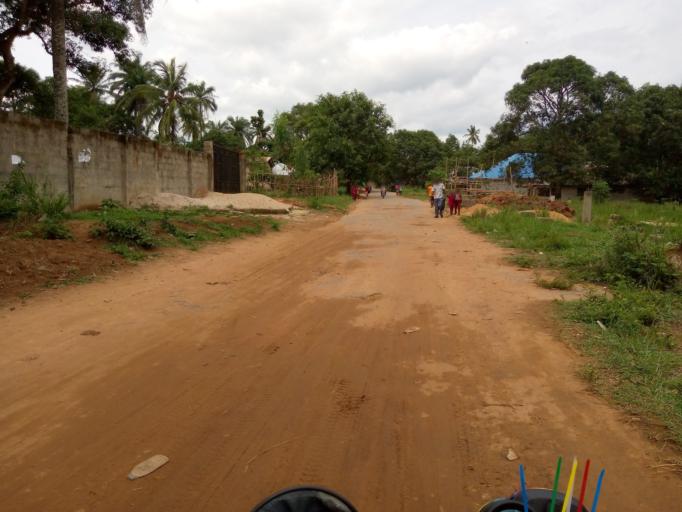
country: SL
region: Western Area
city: Waterloo
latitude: 8.3340
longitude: -13.0155
